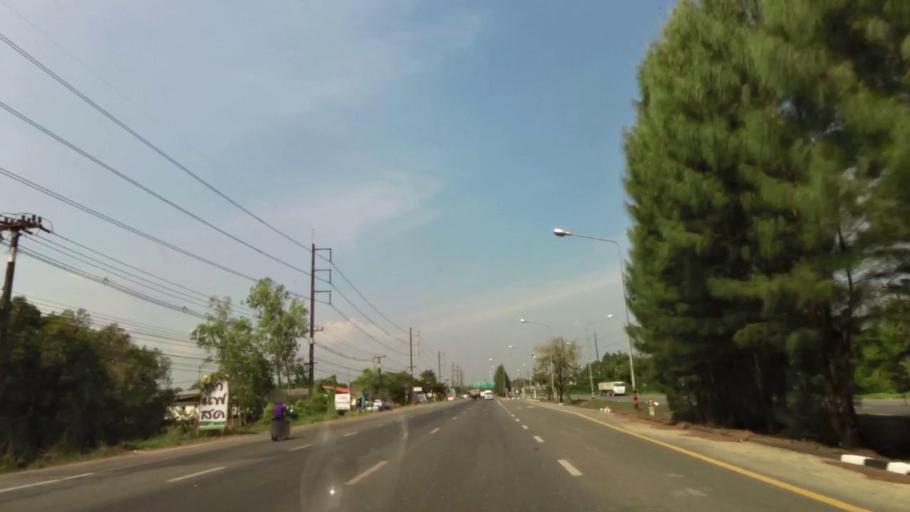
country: TH
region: Chanthaburi
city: Chanthaburi
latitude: 12.6449
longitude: 102.1303
